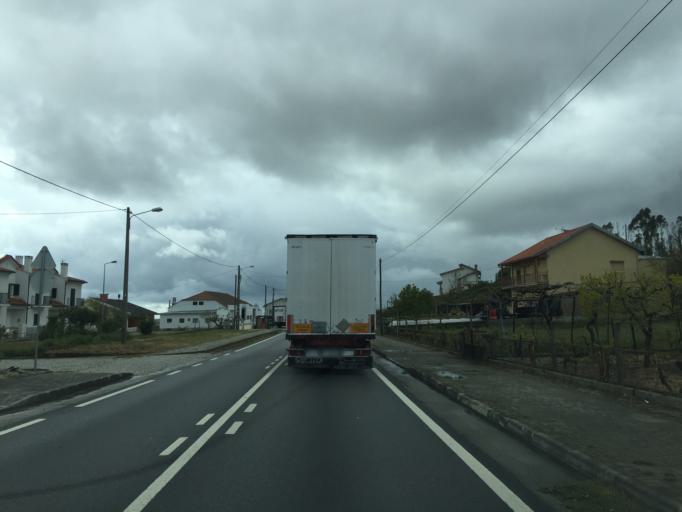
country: PT
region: Coimbra
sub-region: Oliveira do Hospital
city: Oliveira do Hospital
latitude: 40.3153
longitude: -7.9037
